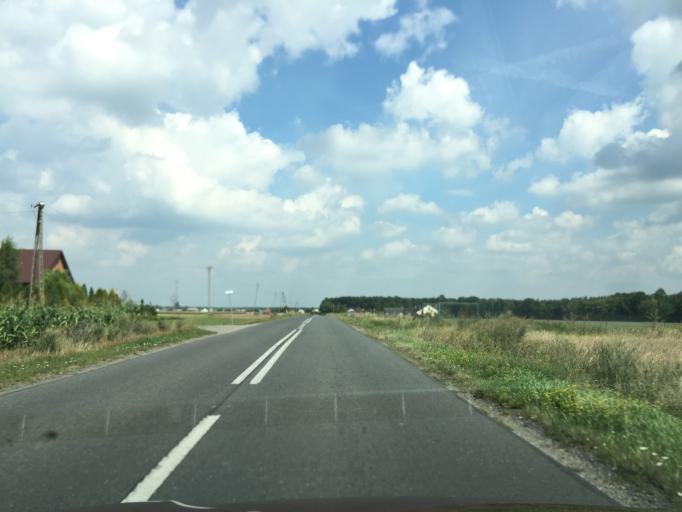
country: PL
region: Greater Poland Voivodeship
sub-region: Powiat kaliski
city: Stawiszyn
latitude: 51.9350
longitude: 18.1482
